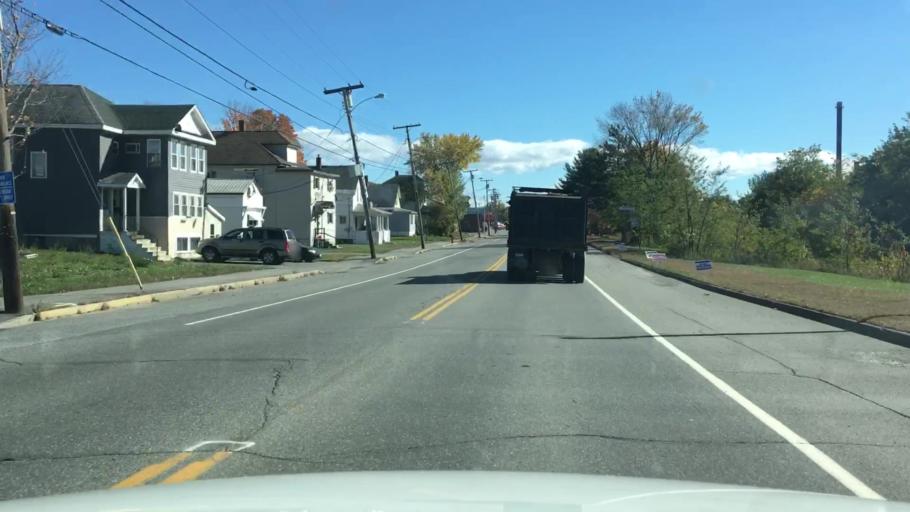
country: US
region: Maine
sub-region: Penobscot County
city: East Millinocket
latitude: 45.6270
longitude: -68.5806
